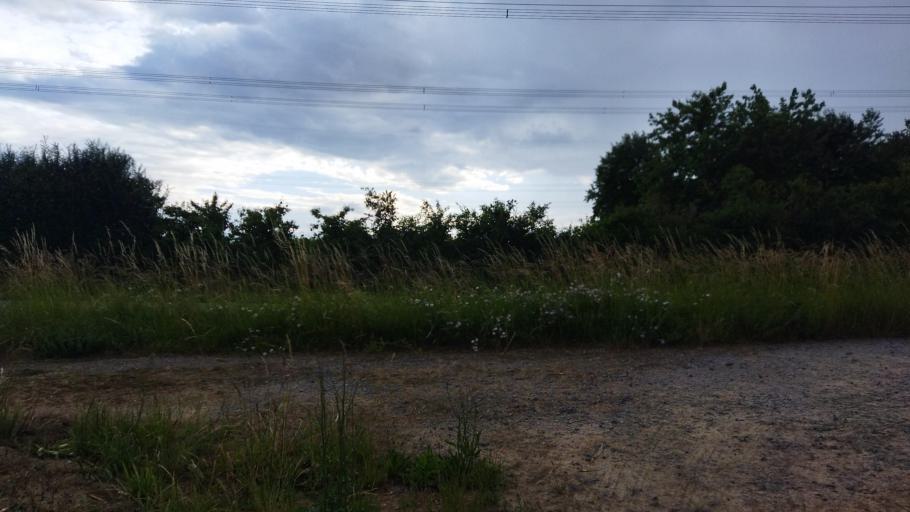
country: DE
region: Baden-Wuerttemberg
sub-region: Regierungsbezirk Stuttgart
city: Talheim
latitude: 49.0929
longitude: 9.1772
